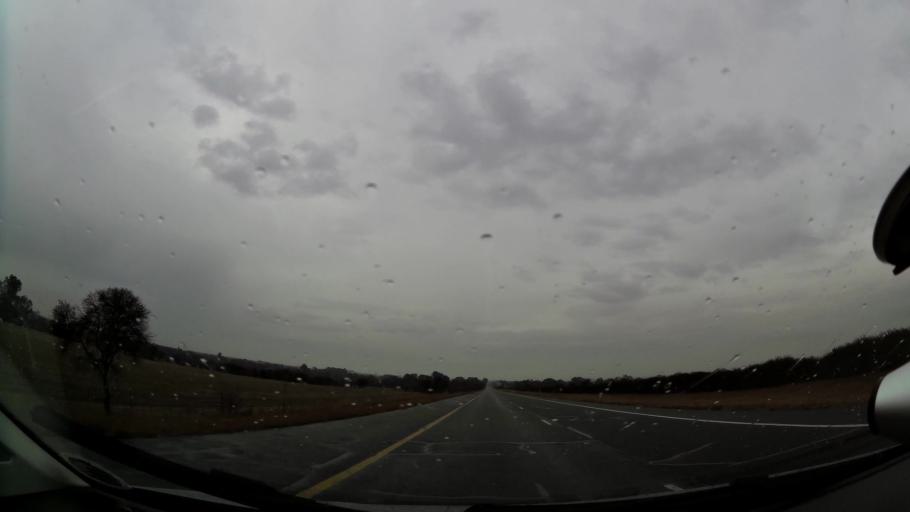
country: ZA
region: Orange Free State
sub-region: Fezile Dabi District Municipality
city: Sasolburg
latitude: -26.7666
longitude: 27.6696
